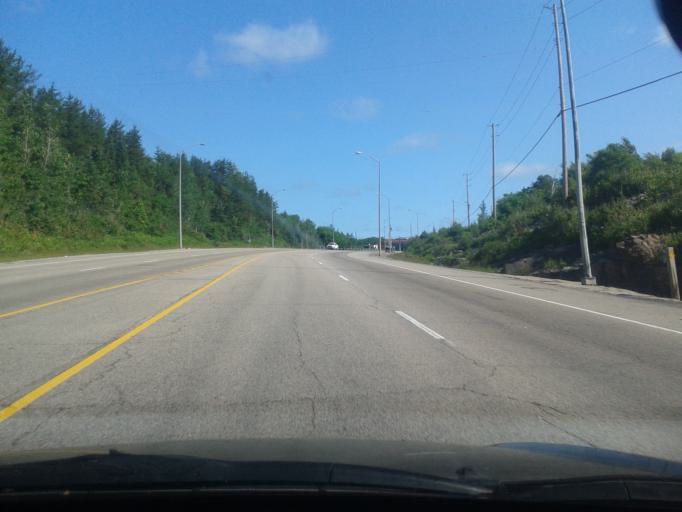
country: CA
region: Ontario
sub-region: Nipissing District
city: North Bay
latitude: 46.3438
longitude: -79.4709
